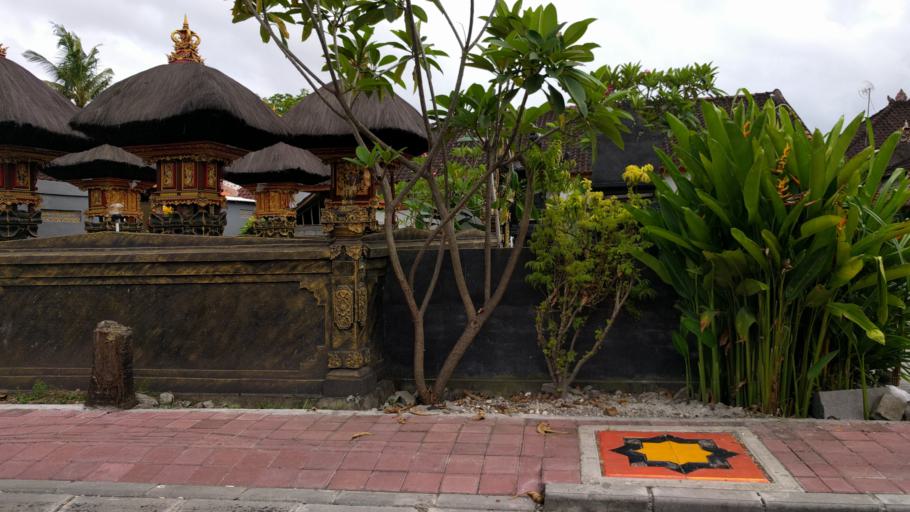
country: ID
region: Bali
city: Kuta
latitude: -8.6729
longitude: 115.1536
